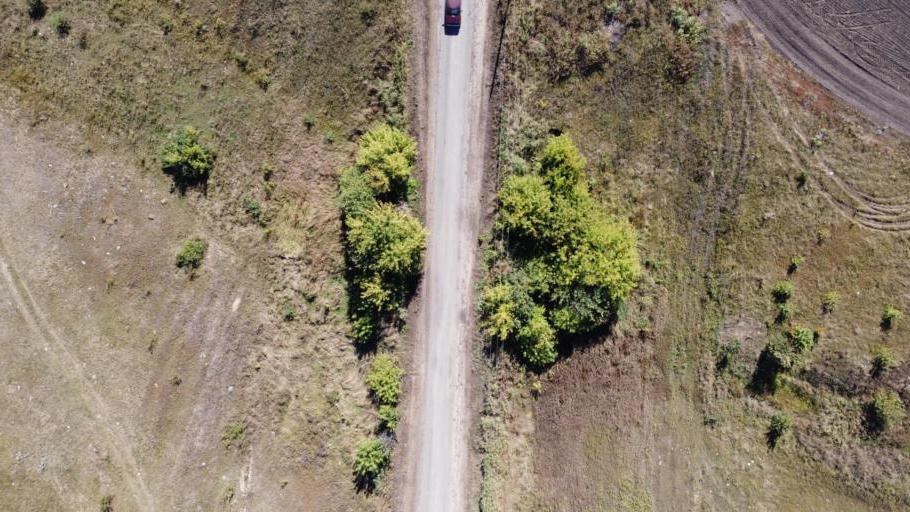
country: RU
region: Kursk
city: Kshenskiy
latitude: 51.8701
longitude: 37.6826
